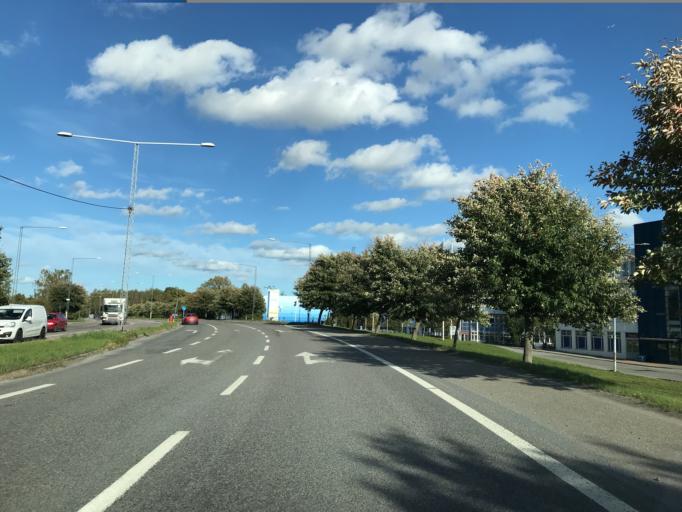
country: SE
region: Stockholm
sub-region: Huddinge Kommun
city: Segeltorp
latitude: 59.2815
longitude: 17.9187
